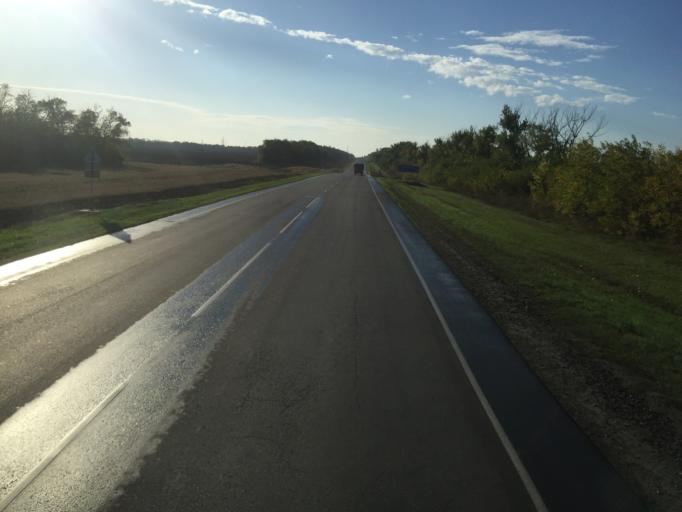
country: RU
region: Rostov
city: Mechetinskaya
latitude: 46.7516
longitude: 40.4608
